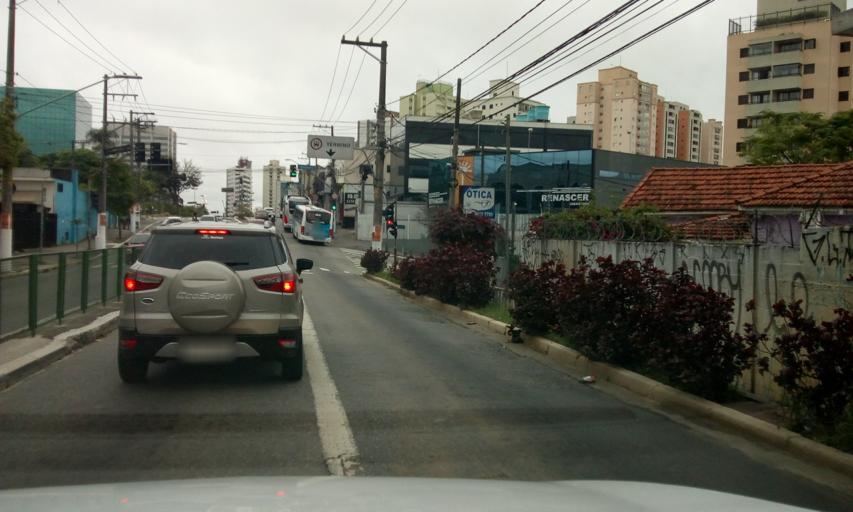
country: BR
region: Sao Paulo
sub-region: Diadema
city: Diadema
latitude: -23.6388
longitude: -46.6413
